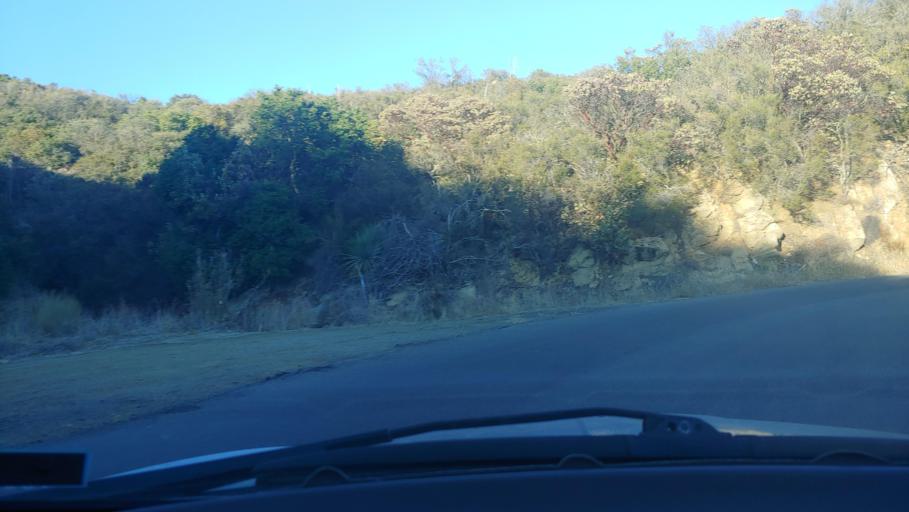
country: US
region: California
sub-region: Santa Barbara County
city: Goleta
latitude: 34.5190
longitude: -119.7914
